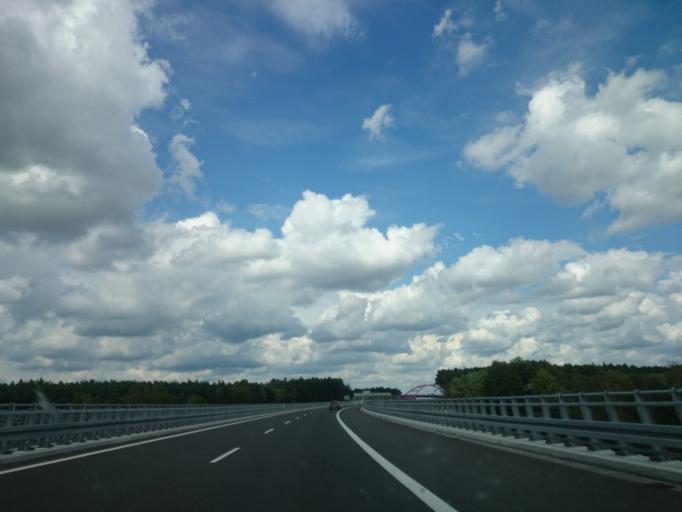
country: PL
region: Lubusz
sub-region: Powiat miedzyrzecki
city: Miedzyrzecz
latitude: 52.4125
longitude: 15.5438
